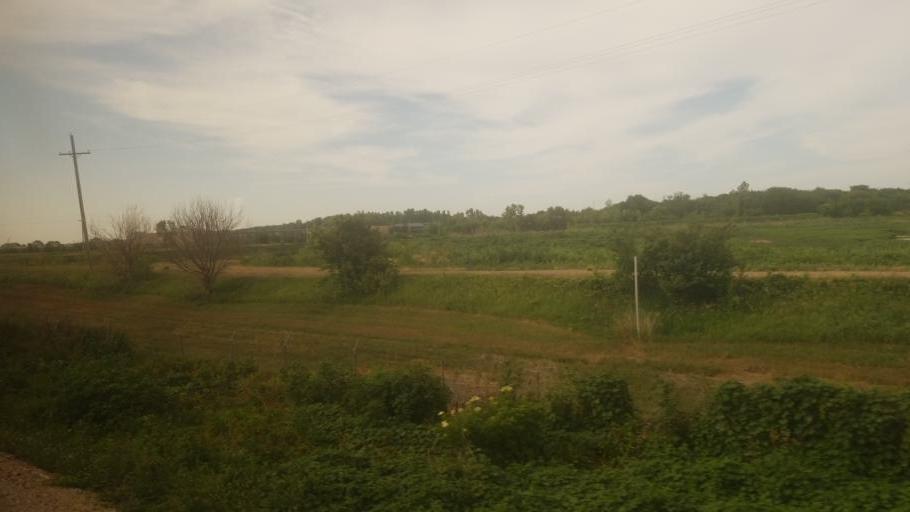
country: US
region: Kansas
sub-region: Douglas County
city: Lawrence
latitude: 38.9530
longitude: -95.1910
